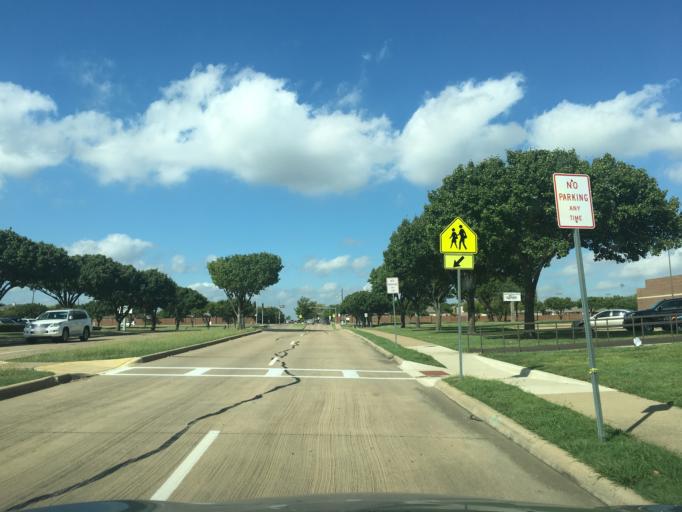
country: US
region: Texas
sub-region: Dallas County
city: Sachse
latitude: 32.9581
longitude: -96.5812
